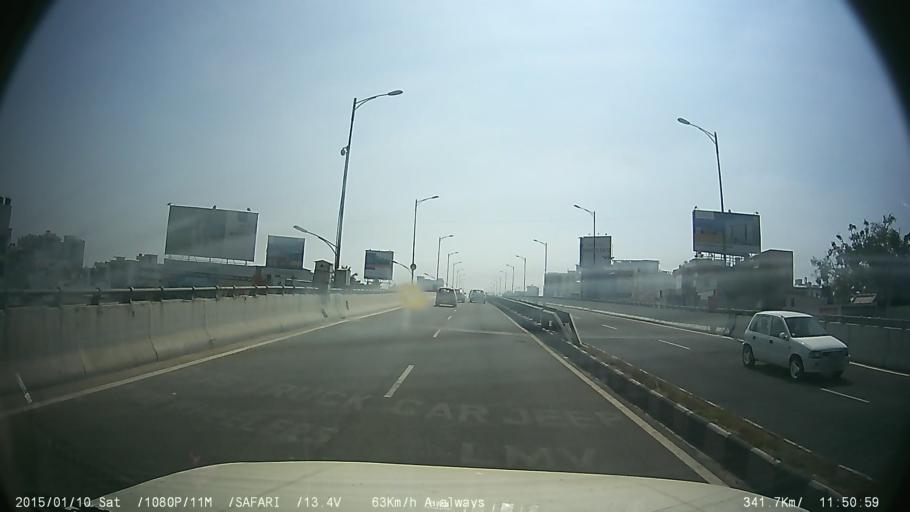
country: IN
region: Karnataka
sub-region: Bangalore Urban
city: Bangalore
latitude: 12.9084
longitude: 77.6281
